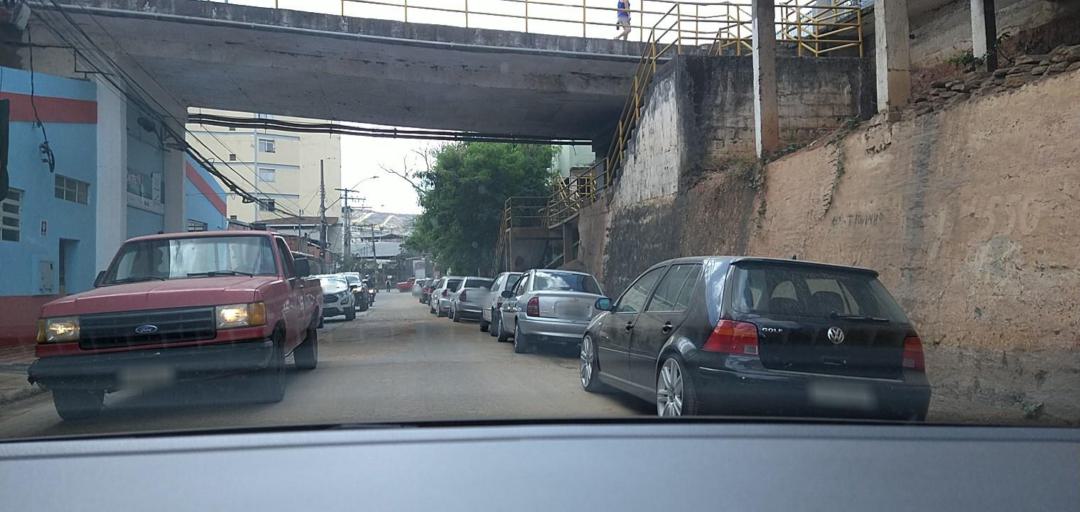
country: BR
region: Minas Gerais
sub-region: Ponte Nova
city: Ponte Nova
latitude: -20.4082
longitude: -42.8959
